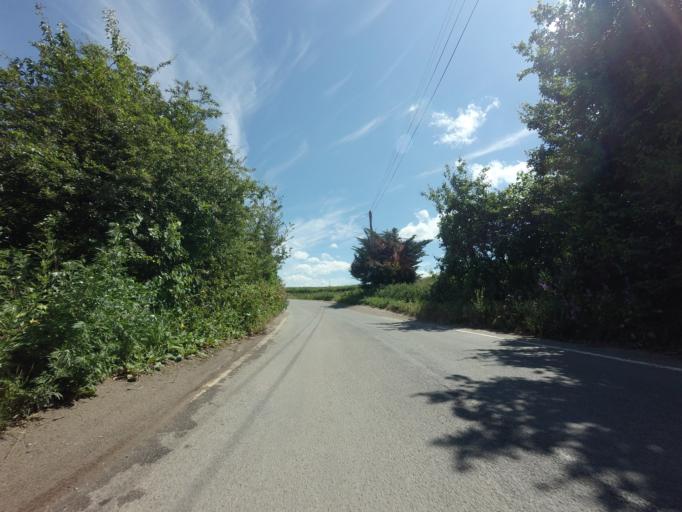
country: GB
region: England
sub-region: Medway
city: High Halstow
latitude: 51.4493
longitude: 0.5508
